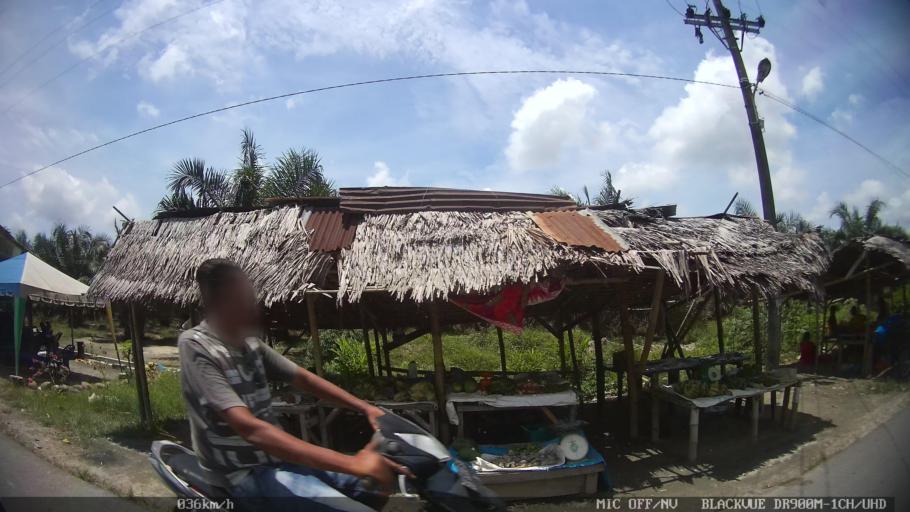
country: ID
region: North Sumatra
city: Percut
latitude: 3.5421
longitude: 98.8652
